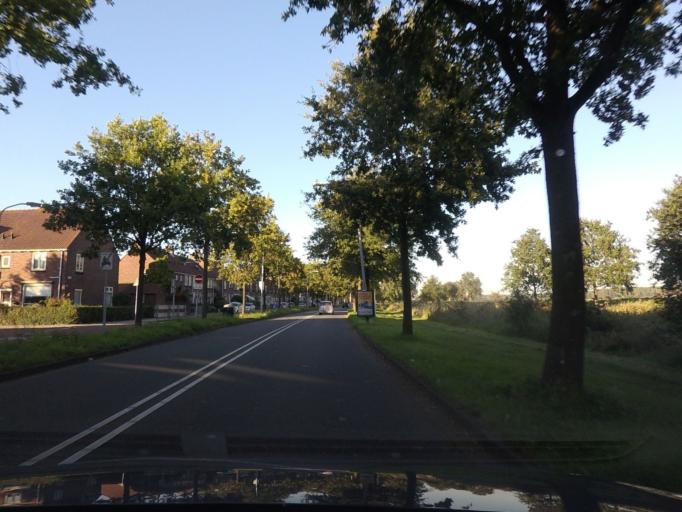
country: NL
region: North Holland
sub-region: Gemeente Bloemendaal
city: Bloemendaal
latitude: 52.4149
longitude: 4.6575
